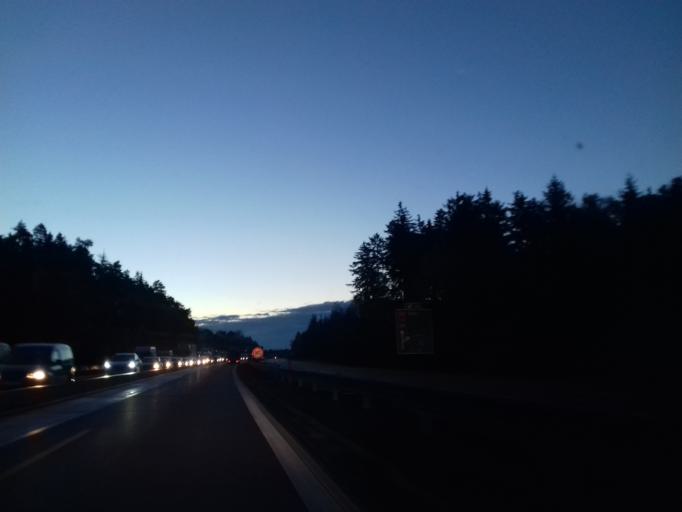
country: CZ
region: South Moravian
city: Zbraslav
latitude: 49.2678
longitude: 16.2901
